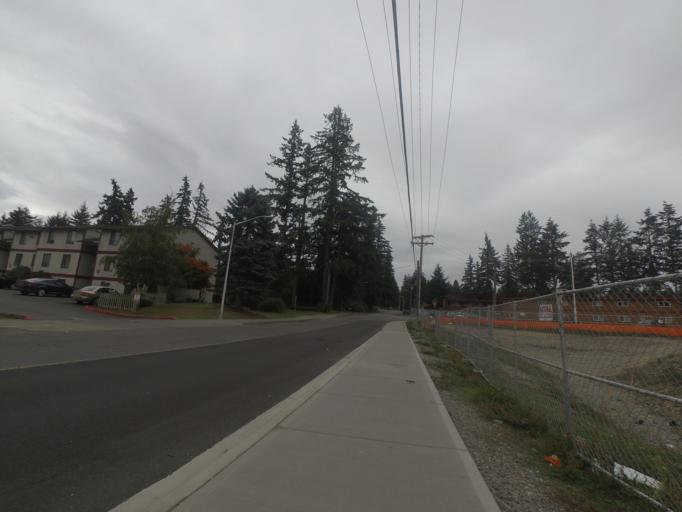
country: US
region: Washington
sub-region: Pierce County
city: McChord Air Force Base
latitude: 47.1420
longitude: -122.5020
